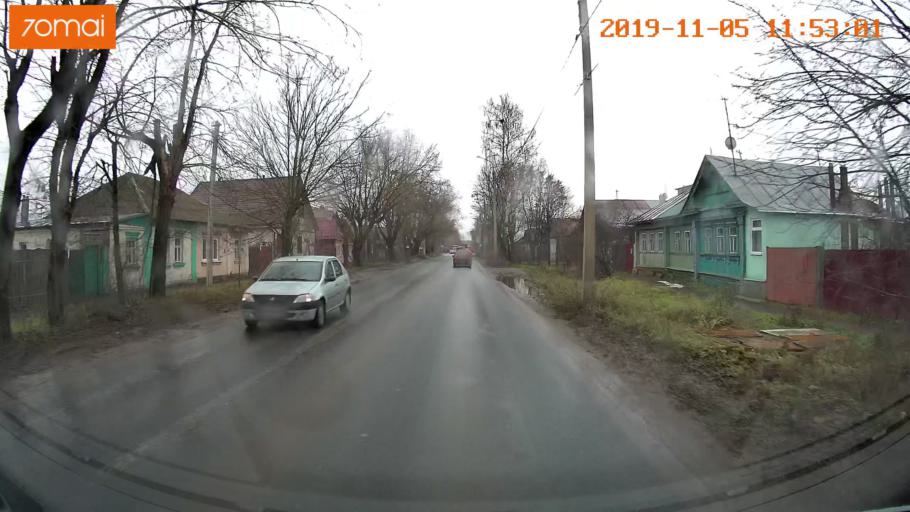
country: RU
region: Ivanovo
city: Bogorodskoye
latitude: 56.9967
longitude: 41.0301
